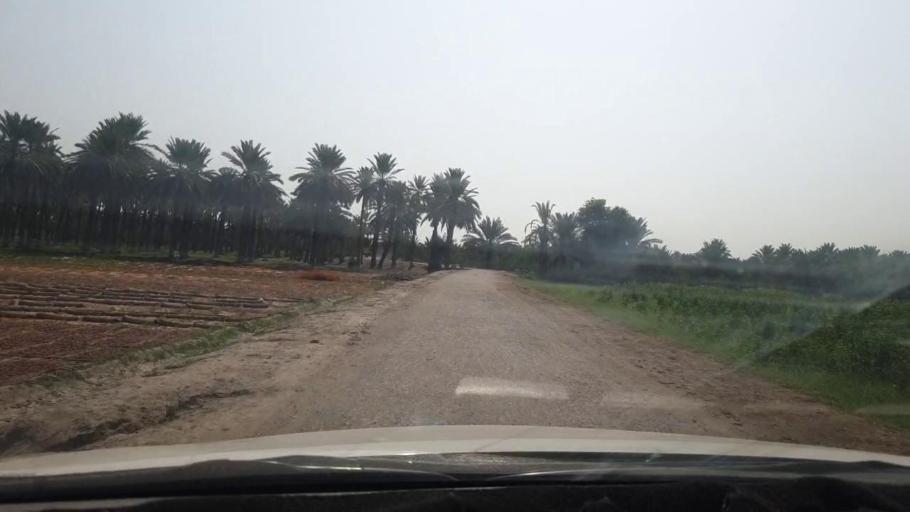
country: PK
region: Sindh
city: Rohri
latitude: 27.6111
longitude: 68.8931
